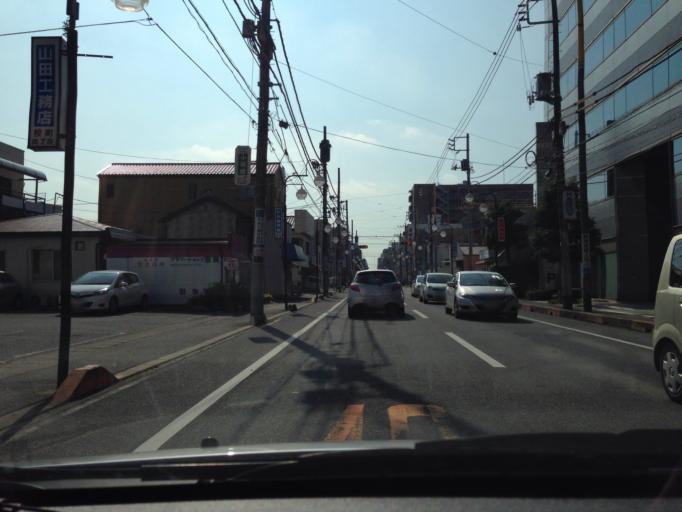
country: JP
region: Ibaraki
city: Naka
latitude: 36.0799
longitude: 140.1974
